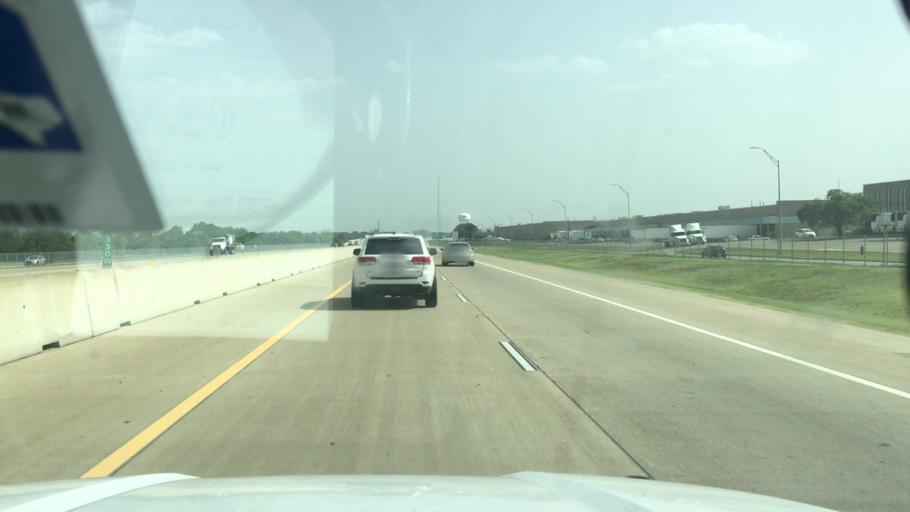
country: US
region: Texas
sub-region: Dallas County
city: Grand Prairie
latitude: 32.7373
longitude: -97.0199
